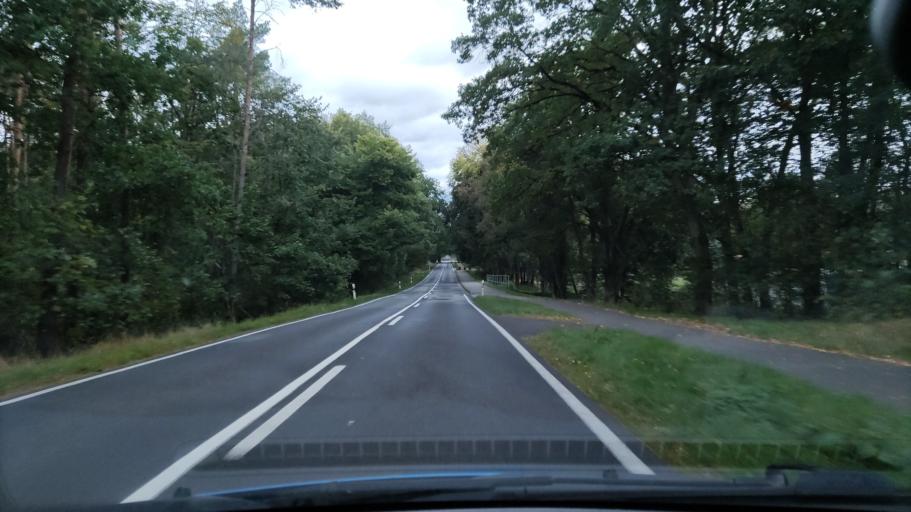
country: DE
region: Mecklenburg-Vorpommern
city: Lubtheen
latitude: 53.3818
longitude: 10.9675
